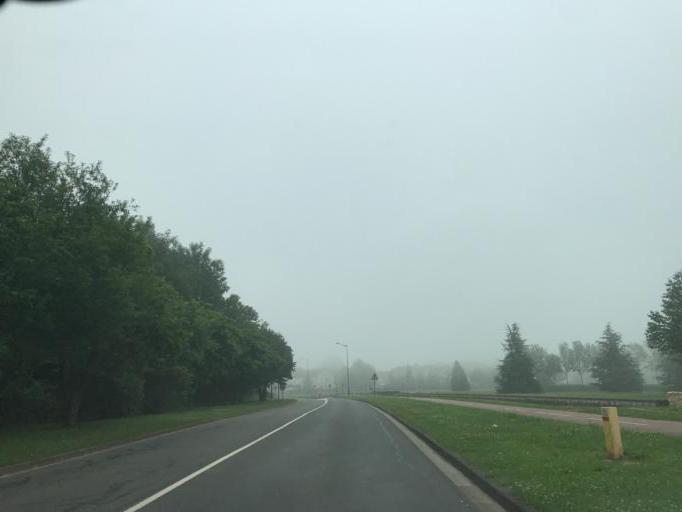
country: FR
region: Ile-de-France
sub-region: Departement de Seine-et-Marne
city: Chessy
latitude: 48.8781
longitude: 2.7613
